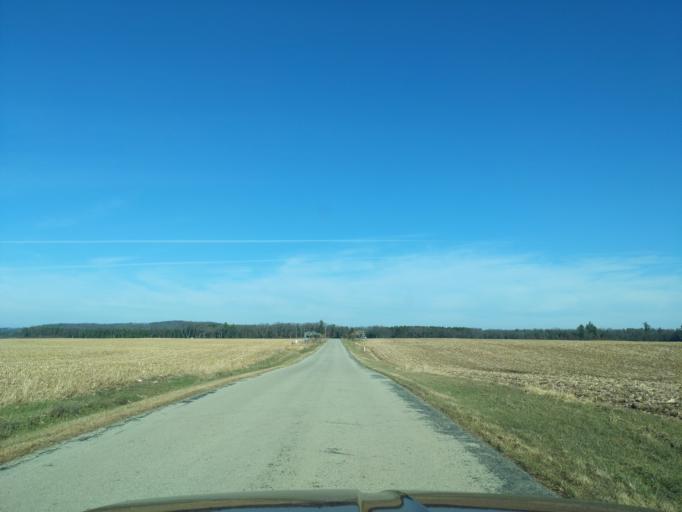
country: US
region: Wisconsin
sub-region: Waushara County
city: Silver Lake
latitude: 44.0923
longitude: -89.1739
